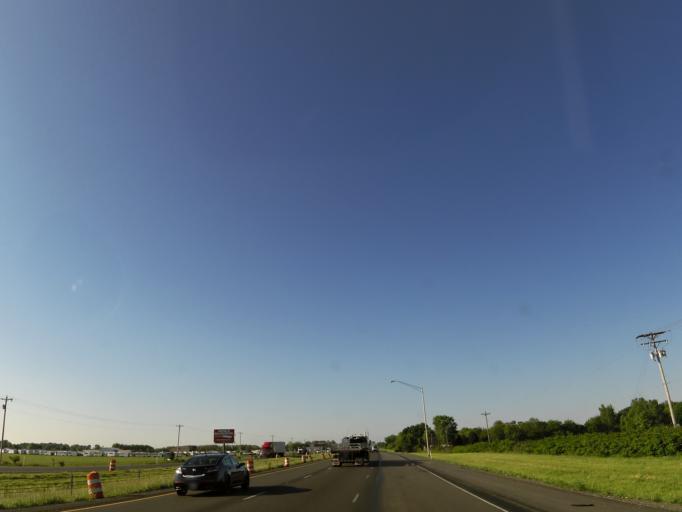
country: US
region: Indiana
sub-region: Jackson County
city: Seymour
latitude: 38.9539
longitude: -85.8437
